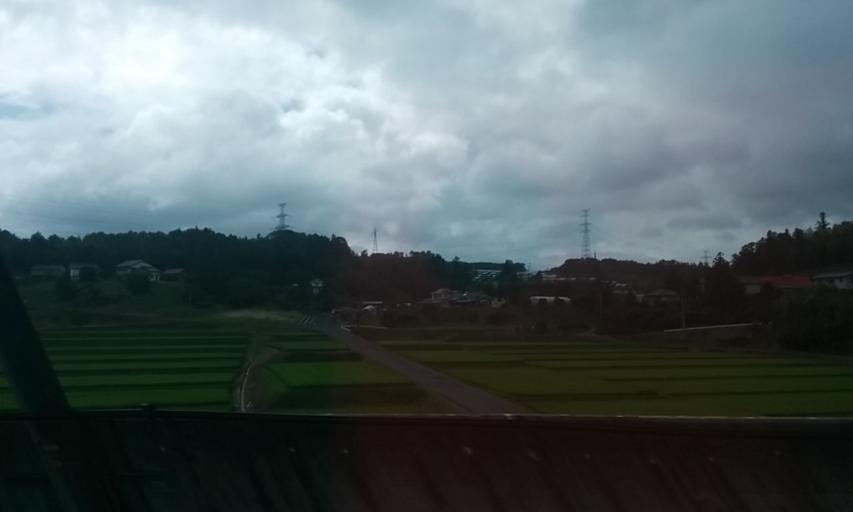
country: JP
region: Fukushima
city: Motomiya
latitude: 37.5160
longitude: 140.4321
